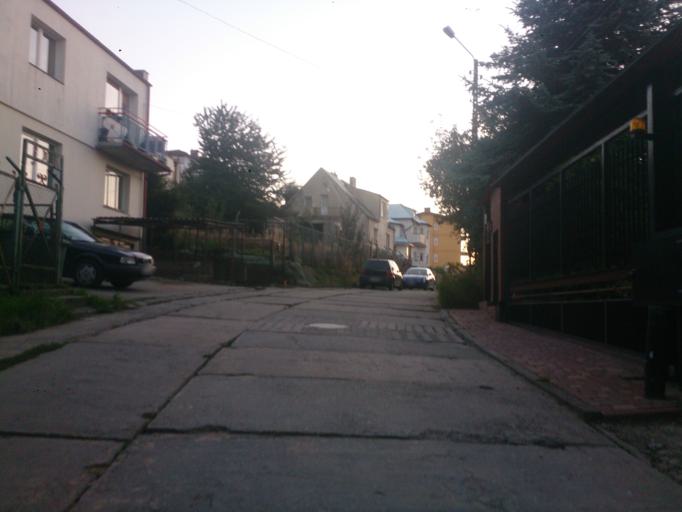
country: PL
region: Pomeranian Voivodeship
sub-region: Gdynia
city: Gdynia
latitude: 54.4784
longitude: 18.5279
